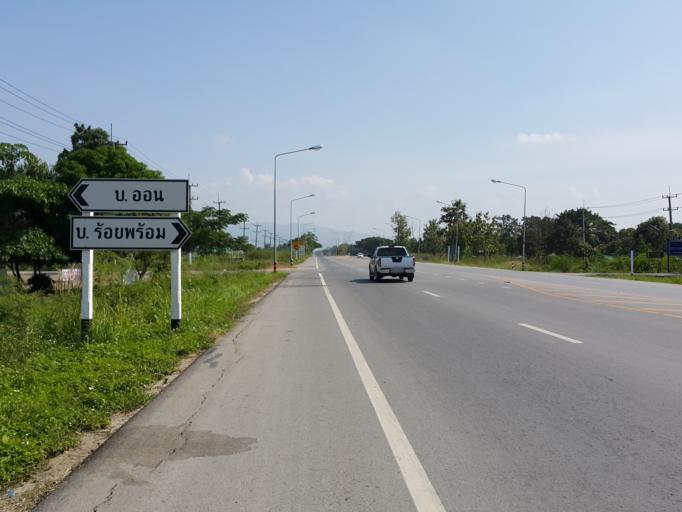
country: TH
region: Chiang Mai
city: San Kamphaeng
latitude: 18.7284
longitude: 99.0996
